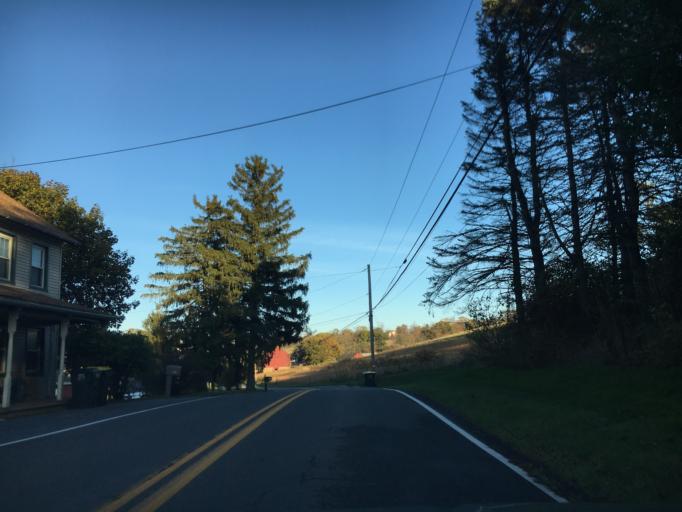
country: US
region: Pennsylvania
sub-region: Lehigh County
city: Laurys Station
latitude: 40.7057
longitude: -75.5621
